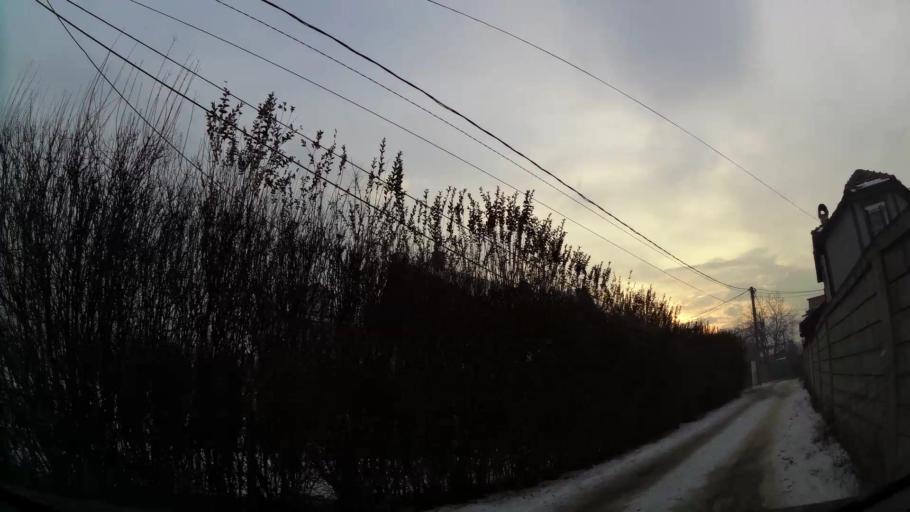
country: MK
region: Suto Orizari
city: Suto Orizare
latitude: 42.0303
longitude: 21.4218
